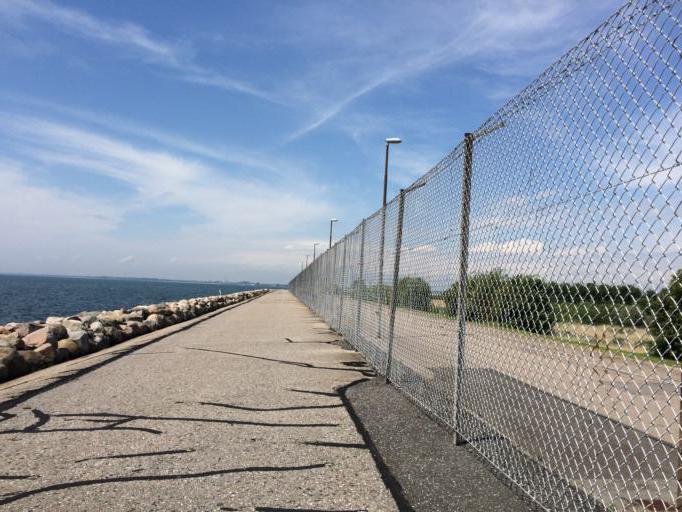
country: DK
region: Capital Region
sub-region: Hvidovre Kommune
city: Hvidovre
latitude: 55.6041
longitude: 12.4517
